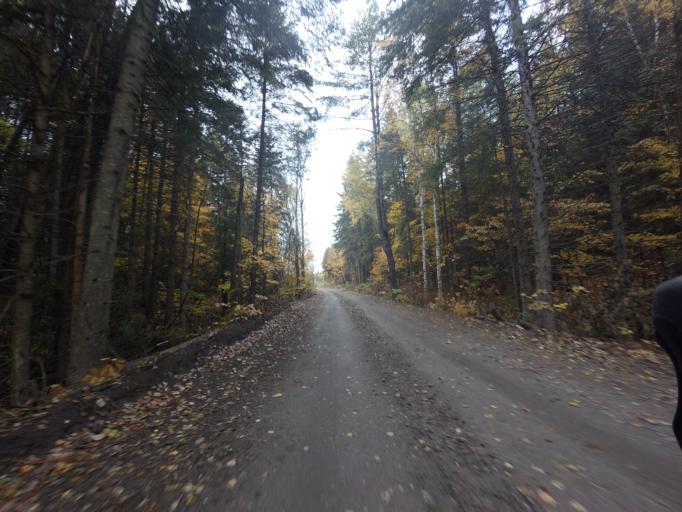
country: CA
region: Ontario
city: Renfrew
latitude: 45.1648
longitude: -76.6825
